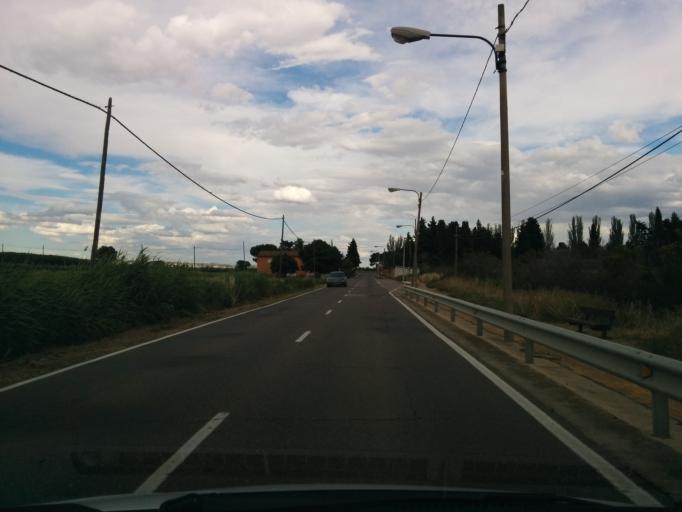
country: ES
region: Aragon
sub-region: Provincia de Zaragoza
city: Puebla de Alfinden
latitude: 41.6438
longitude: -0.8094
